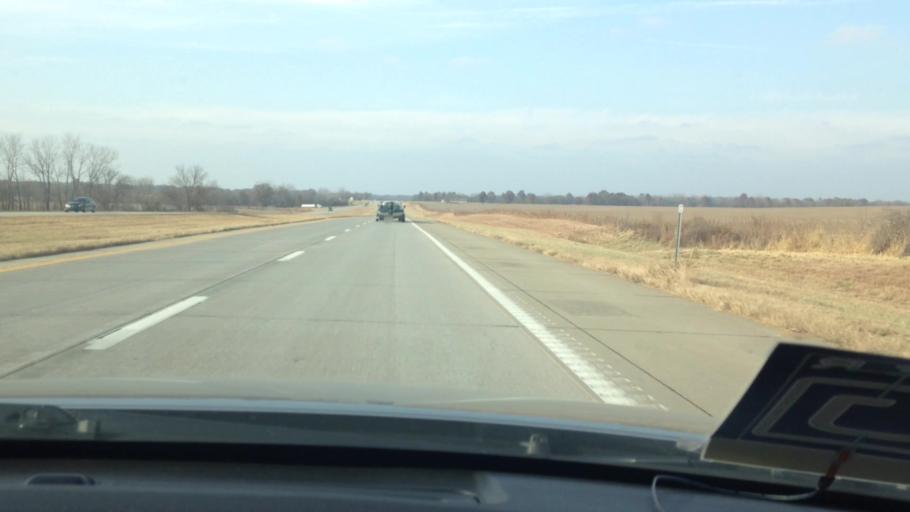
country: US
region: Missouri
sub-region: Henry County
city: Clinton
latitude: 38.4457
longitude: -93.9560
